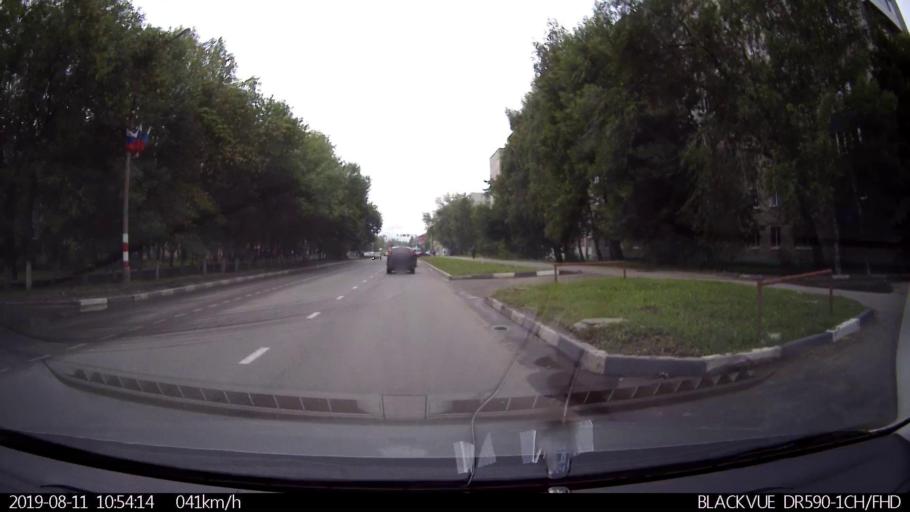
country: RU
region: Ulyanovsk
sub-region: Ulyanovskiy Rayon
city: Ulyanovsk
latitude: 54.2573
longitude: 48.3342
